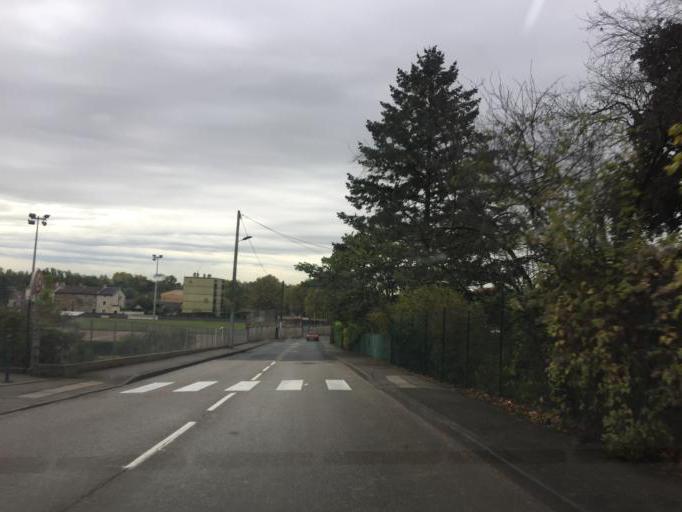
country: FR
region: Rhone-Alpes
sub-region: Departement de l'Ain
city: Miribel
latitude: 45.8226
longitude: 4.9440
